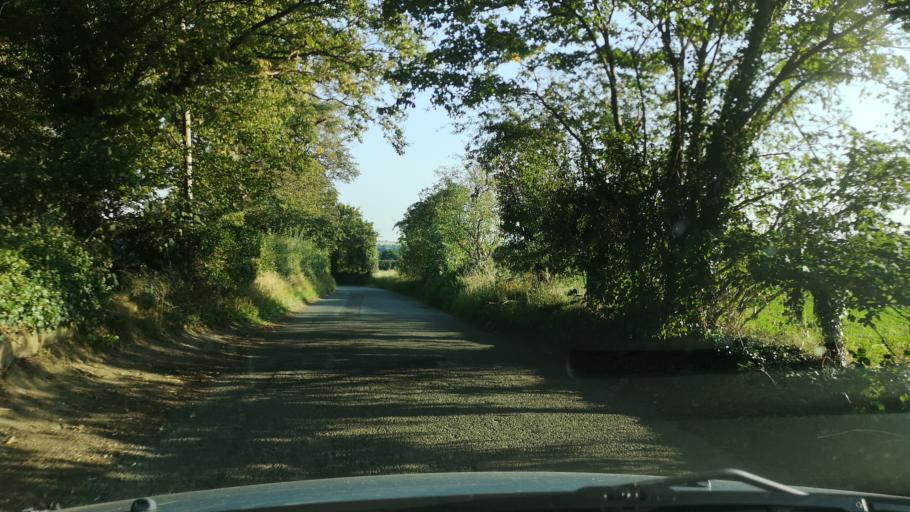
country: GB
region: England
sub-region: City and Borough of Wakefield
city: Low Ackworth
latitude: 53.6555
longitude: -1.3267
